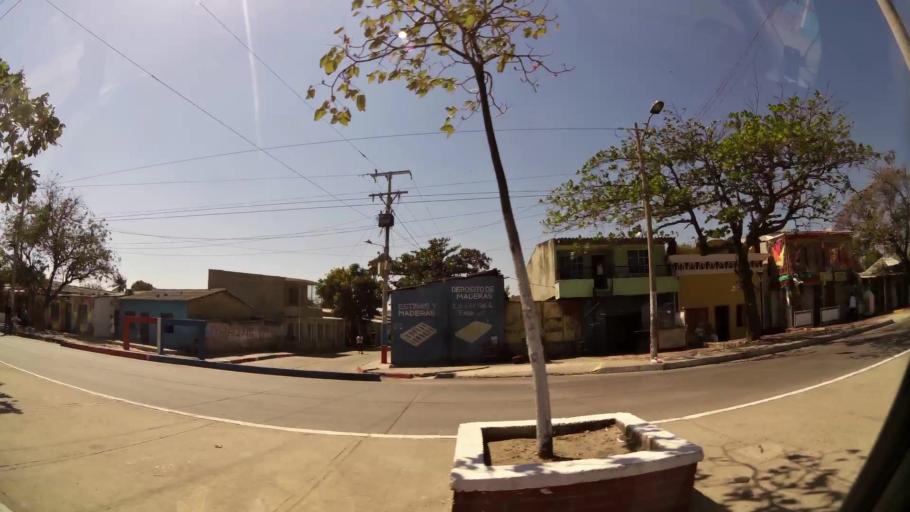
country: CO
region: Atlantico
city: Barranquilla
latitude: 10.9705
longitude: -74.7744
